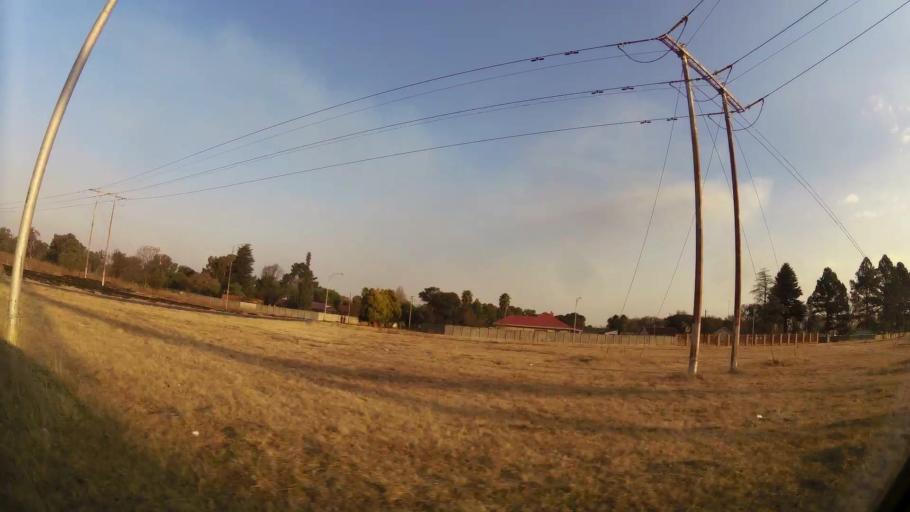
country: ZA
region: Gauteng
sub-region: Ekurhuleni Metropolitan Municipality
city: Springs
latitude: -26.2685
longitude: 28.4176
